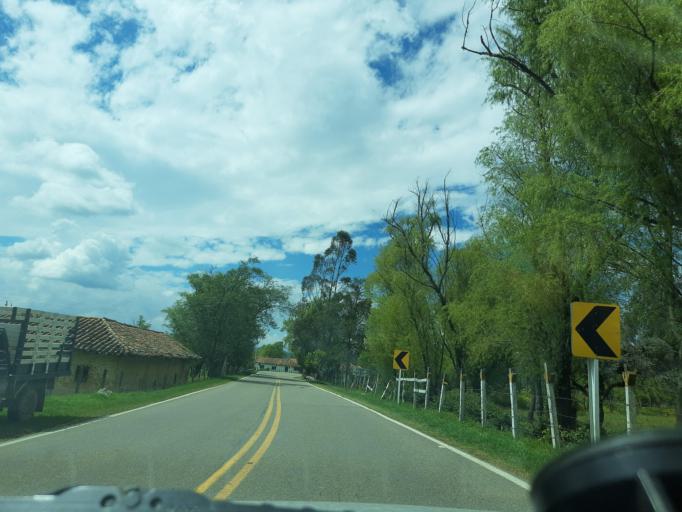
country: CO
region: Boyaca
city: Chiquinquira
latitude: 5.6066
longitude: -73.7249
